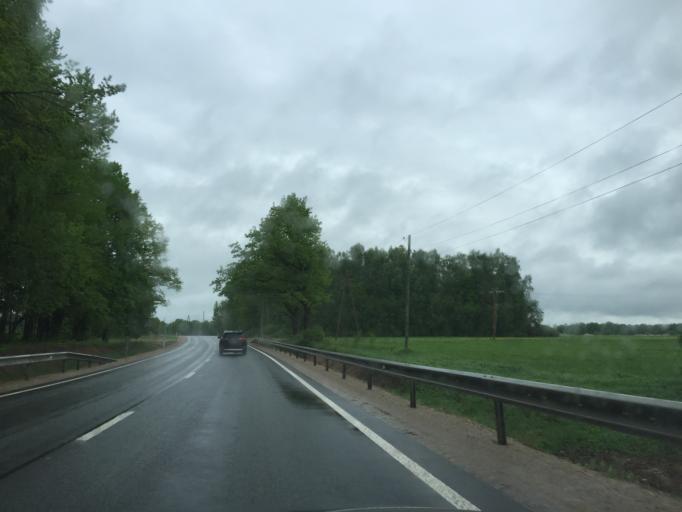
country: LV
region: Ogre
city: Jumprava
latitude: 56.6848
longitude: 24.8974
